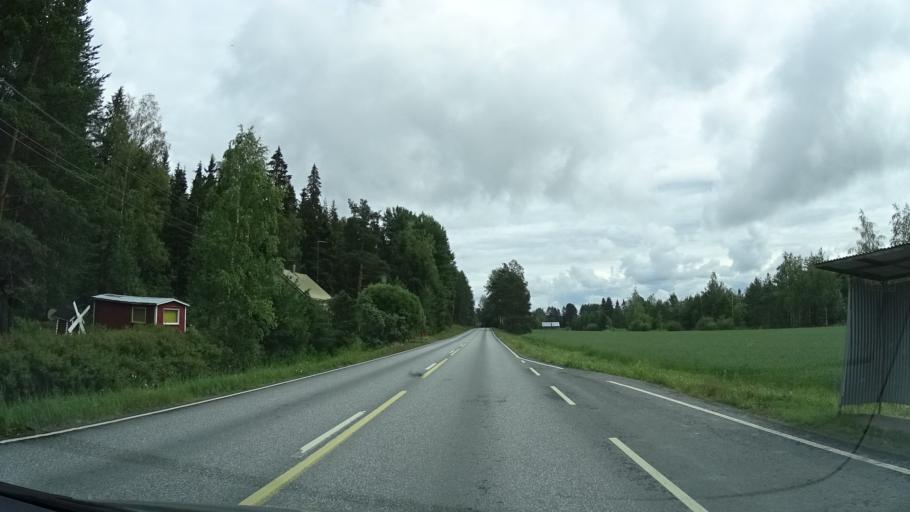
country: FI
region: Haeme
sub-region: Forssa
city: Humppila
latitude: 61.0945
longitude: 23.3660
